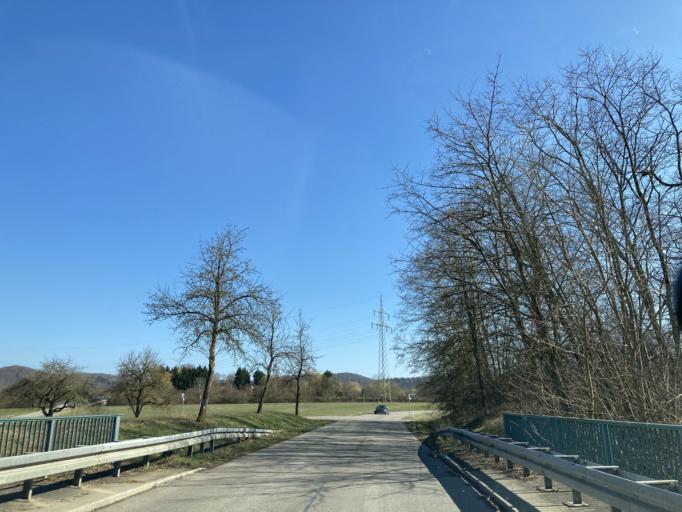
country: DE
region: Baden-Wuerttemberg
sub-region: Tuebingen Region
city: Bodelshausen
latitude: 48.3804
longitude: 8.9867
